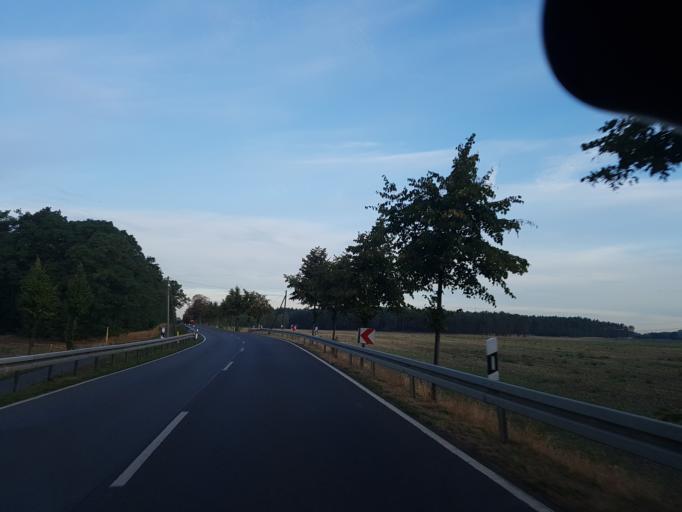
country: DE
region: Brandenburg
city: Finsterwalde
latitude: 51.6497
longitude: 13.6843
